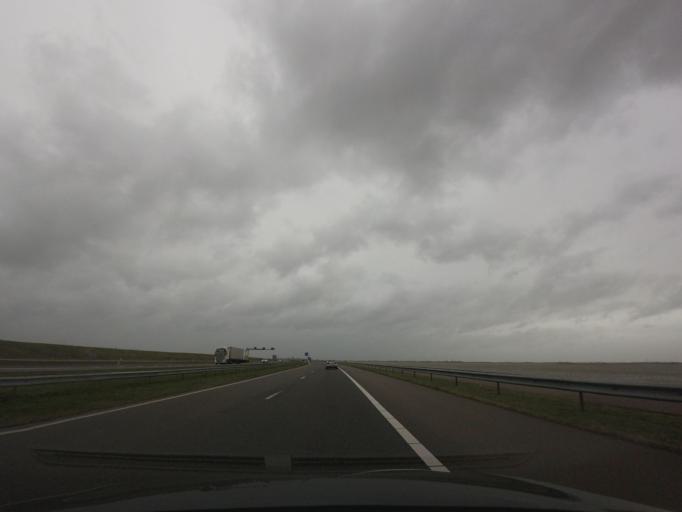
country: NL
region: Friesland
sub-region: Sudwest Fryslan
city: Makkum
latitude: 53.0768
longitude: 5.3489
